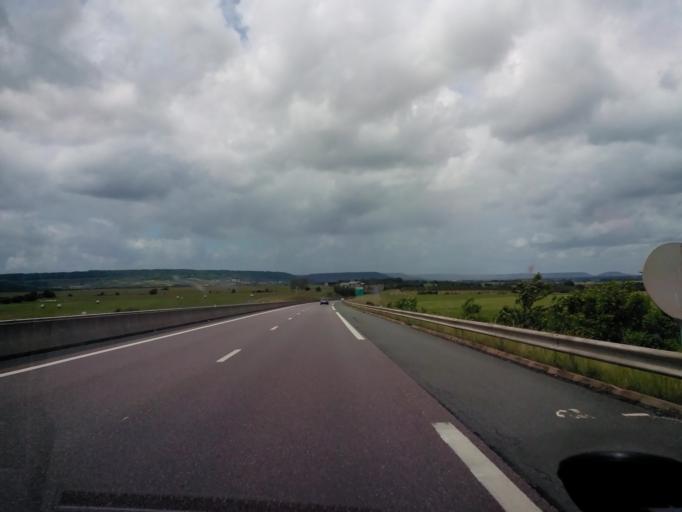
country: FR
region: Lorraine
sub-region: Departement de Meurthe-et-Moselle
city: Colombey-les-Belles
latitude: 48.5409
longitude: 5.9015
